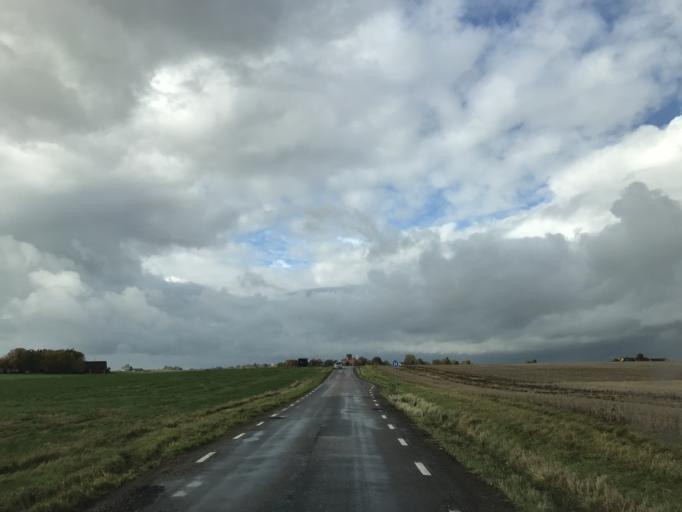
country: SE
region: Skane
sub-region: Svalovs Kommun
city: Svaloev
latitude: 55.9076
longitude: 13.1595
